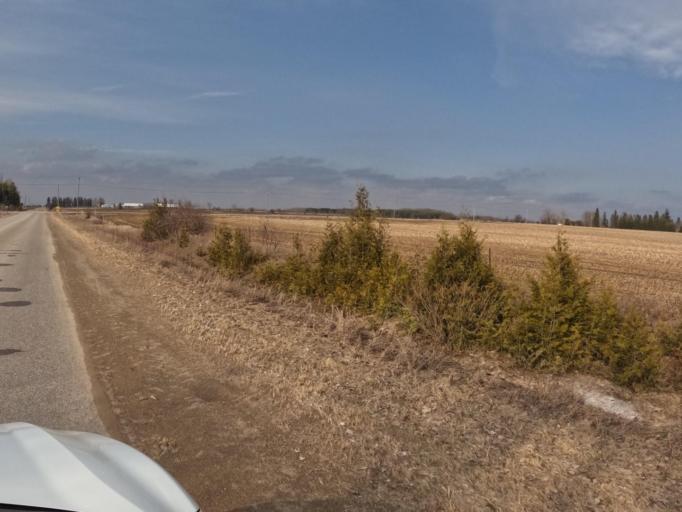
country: CA
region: Ontario
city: Orangeville
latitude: 43.9065
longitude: -80.2863
